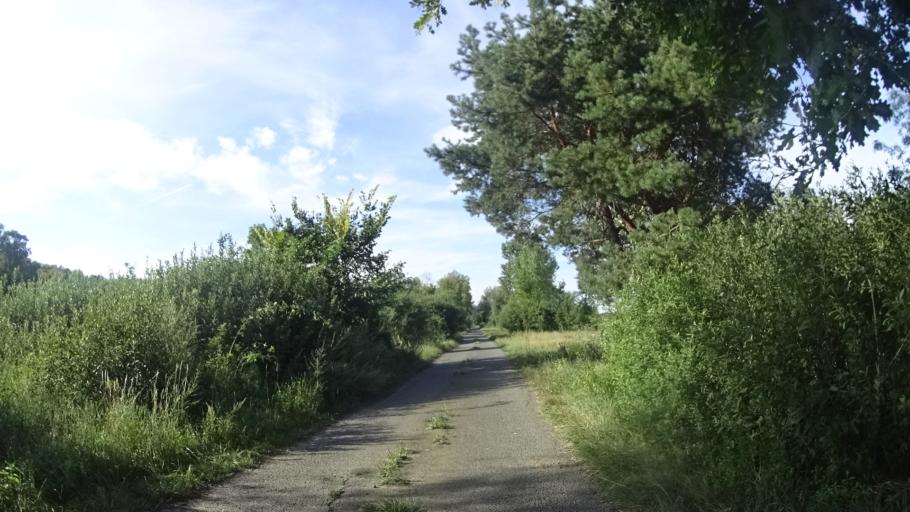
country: AT
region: Lower Austria
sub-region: Politischer Bezirk Ganserndorf
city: Drosing
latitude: 48.5752
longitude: 16.9536
